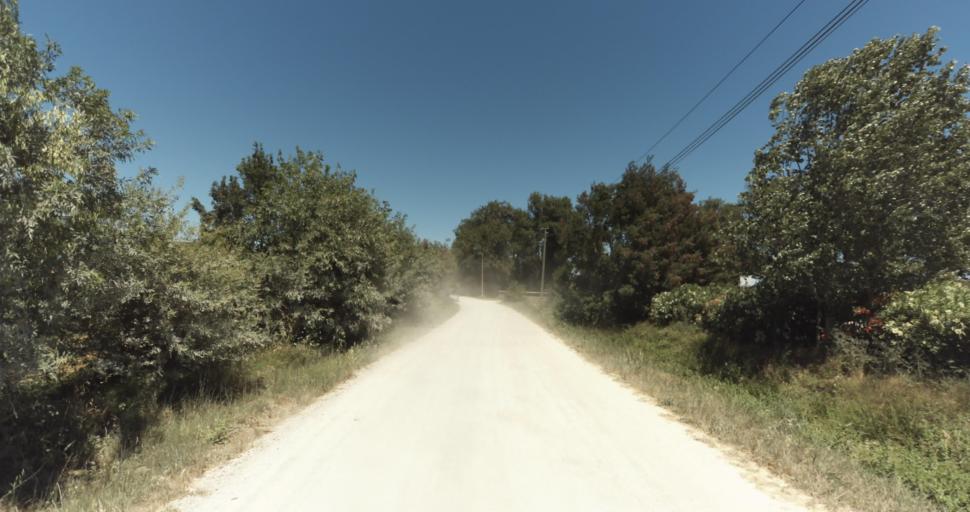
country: FR
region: Provence-Alpes-Cote d'Azur
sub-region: Departement du Var
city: Gassin
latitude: 43.2560
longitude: 6.5762
